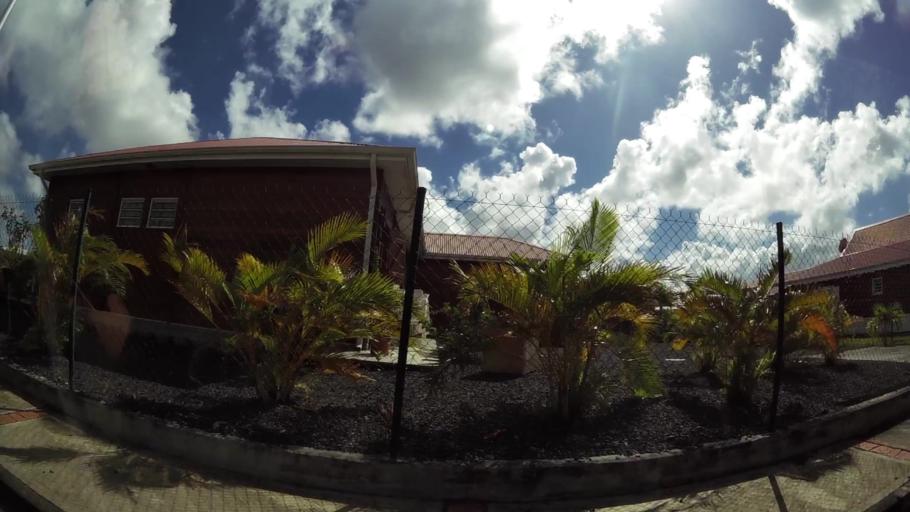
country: GP
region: Guadeloupe
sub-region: Guadeloupe
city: Port-Louis
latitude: 16.4238
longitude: -61.5280
